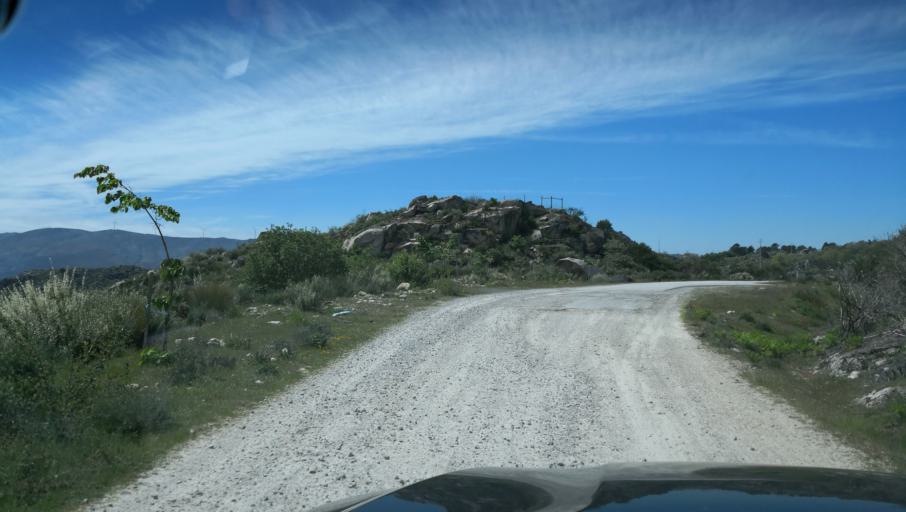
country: PT
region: Vila Real
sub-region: Vila Real
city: Vila Real
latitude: 41.3712
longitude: -7.6749
